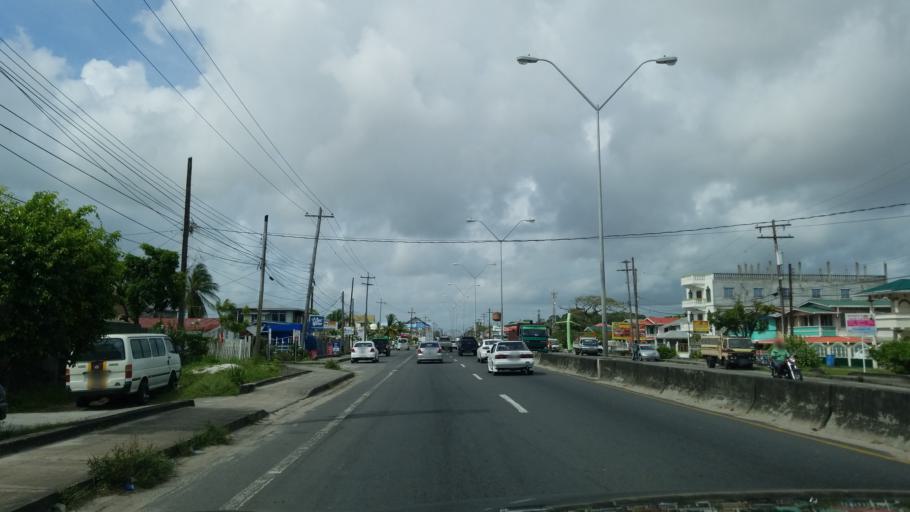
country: GY
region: Demerara-Mahaica
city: Georgetown
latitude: 6.7849
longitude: -58.1690
